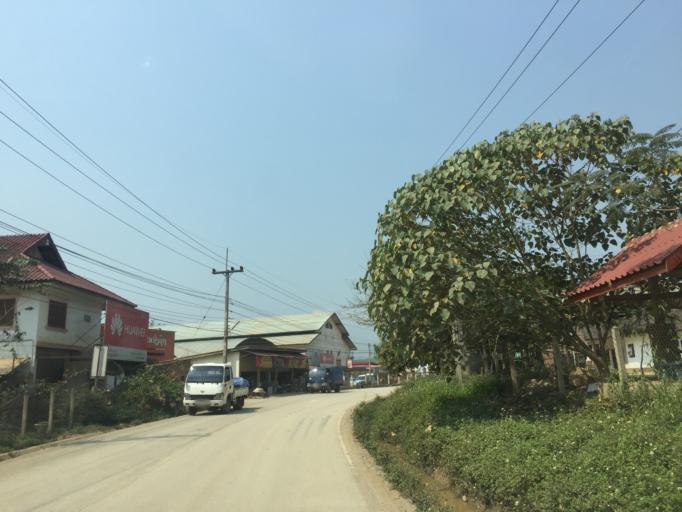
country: LA
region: Oudomxai
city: Muang Xay
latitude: 20.9061
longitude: 101.7634
